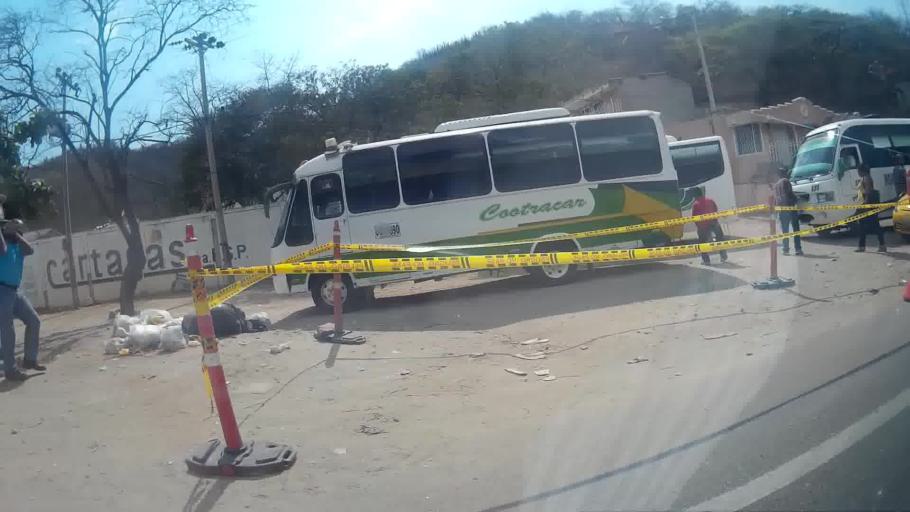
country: CO
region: Magdalena
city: Santa Marta
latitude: 11.2133
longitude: -74.1916
